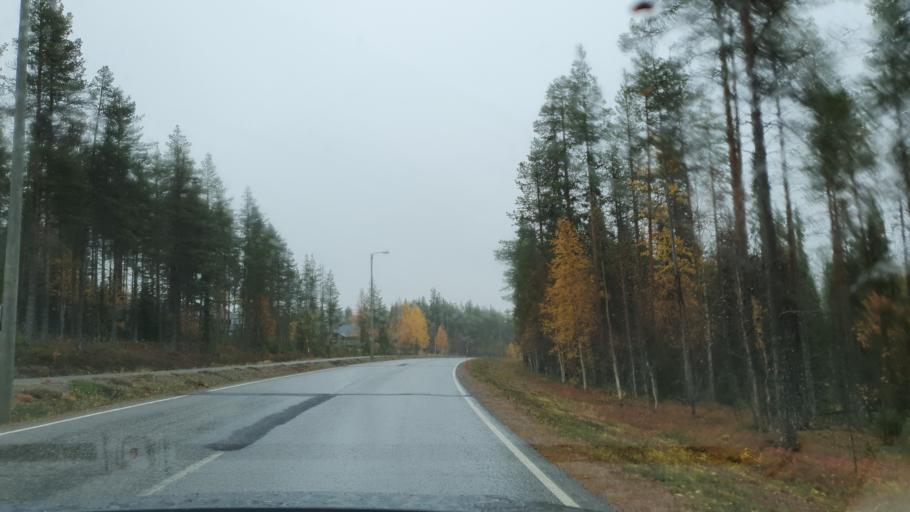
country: FI
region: Lapland
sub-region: Tunturi-Lappi
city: Kolari
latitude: 67.6002
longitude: 24.1249
